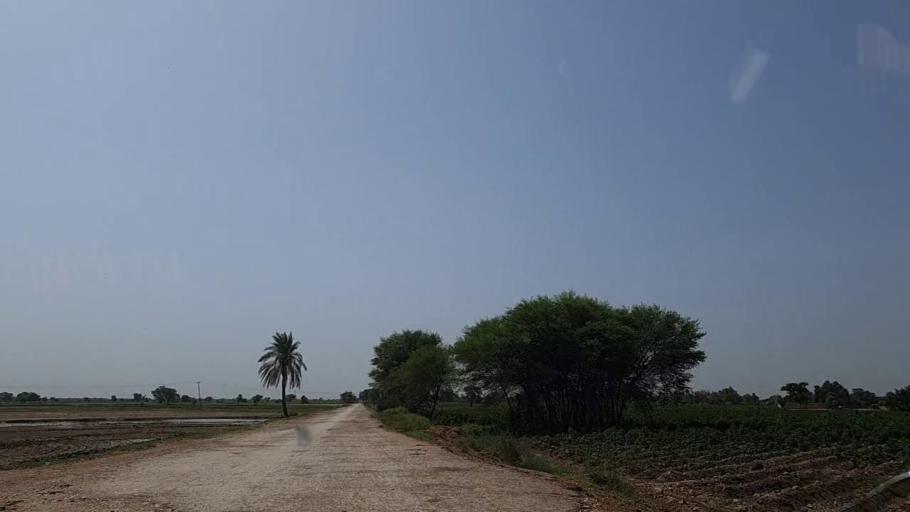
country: PK
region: Sindh
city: Naushahro Firoz
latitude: 26.8491
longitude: 68.0109
